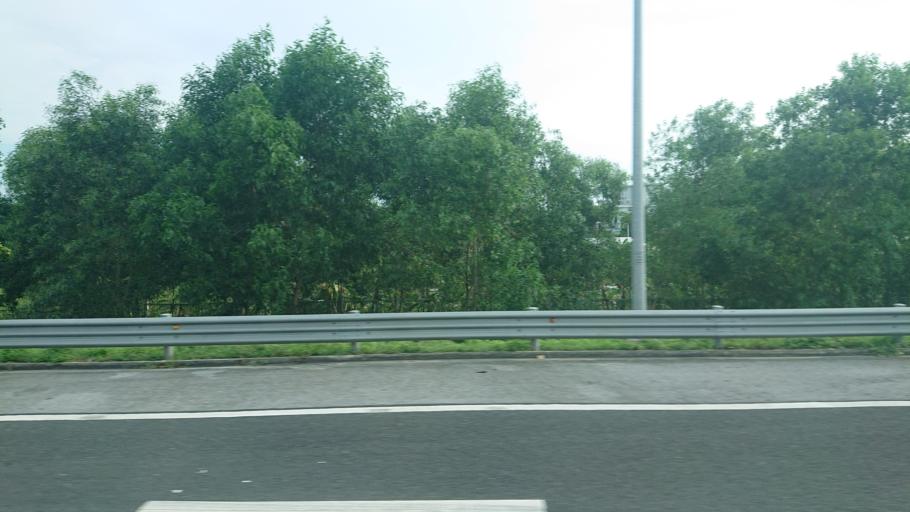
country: VN
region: Hai Phong
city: An Lao
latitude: 20.7901
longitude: 106.5536
